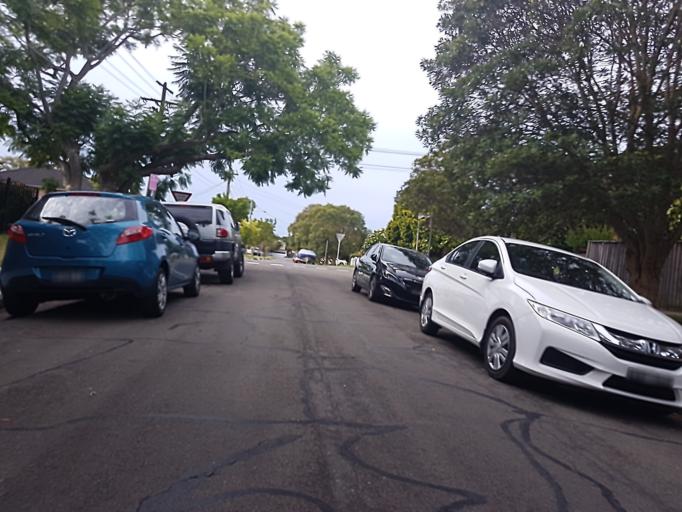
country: AU
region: New South Wales
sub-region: Willoughby
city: Castle Cove
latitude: -33.7977
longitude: 151.2044
